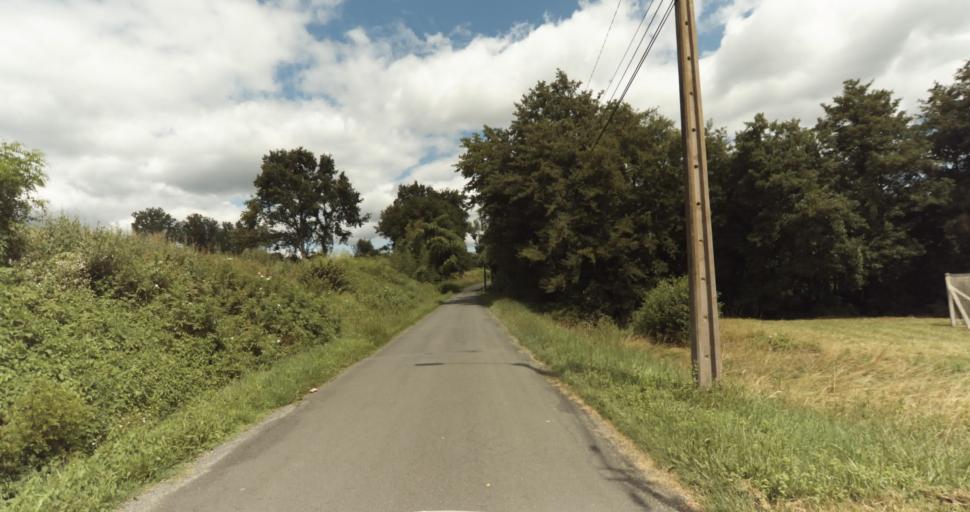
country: FR
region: Aquitaine
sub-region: Departement de la Gironde
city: Bazas
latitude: 44.4382
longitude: -0.2194
